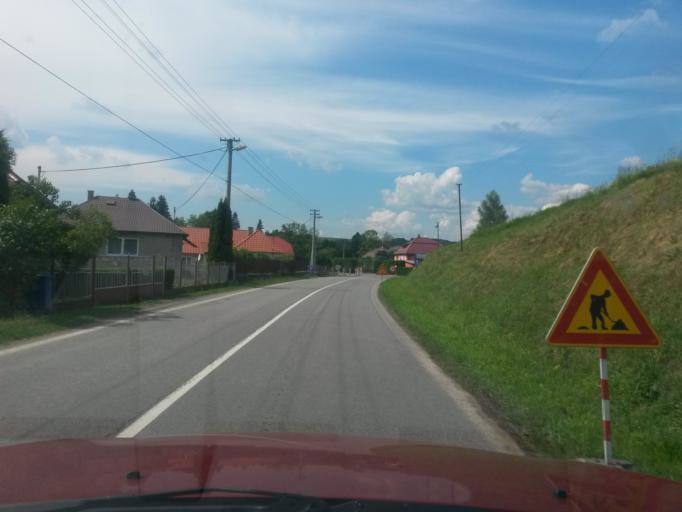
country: UA
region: Zakarpattia
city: Velykyi Bereznyi
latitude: 48.9018
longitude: 22.3862
